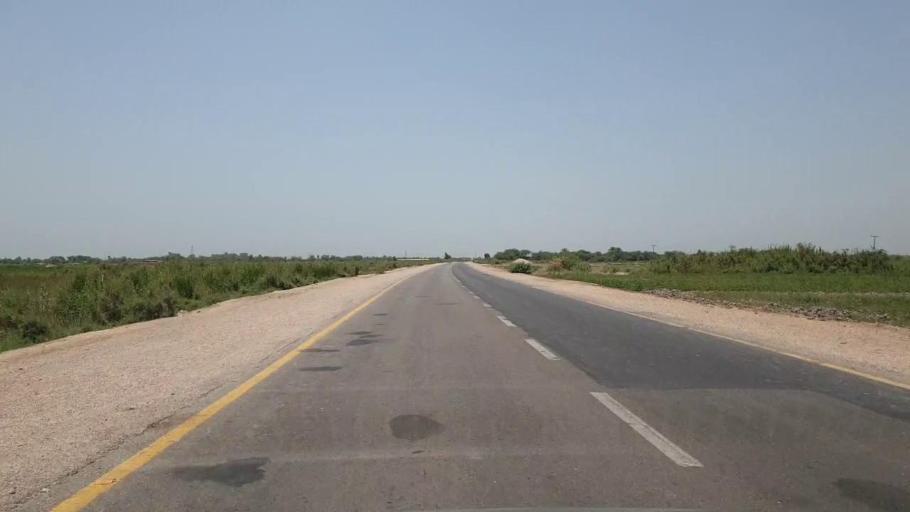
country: PK
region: Sindh
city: Sakrand
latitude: 26.1265
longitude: 68.3800
